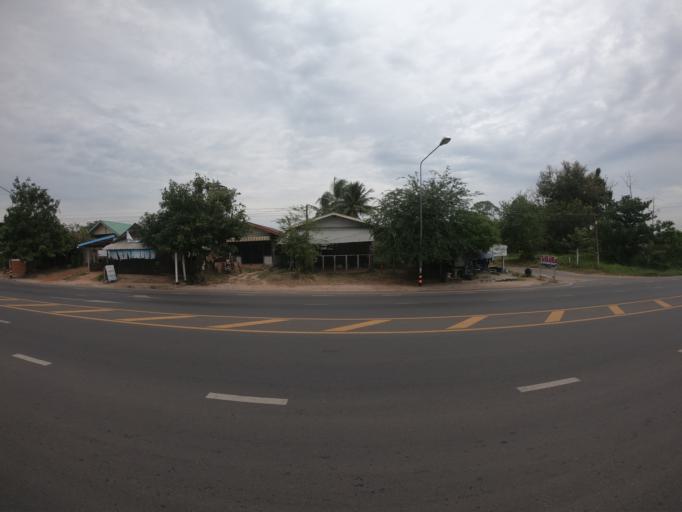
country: TH
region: Roi Et
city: Chiang Khwan
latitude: 16.1477
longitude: 103.8593
